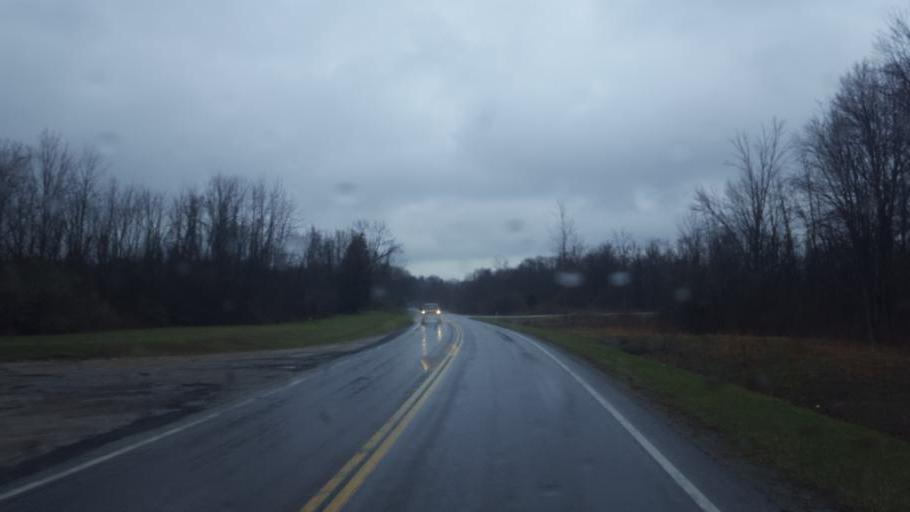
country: US
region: Ohio
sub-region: Franklin County
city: Westerville
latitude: 40.1901
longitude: -82.9438
